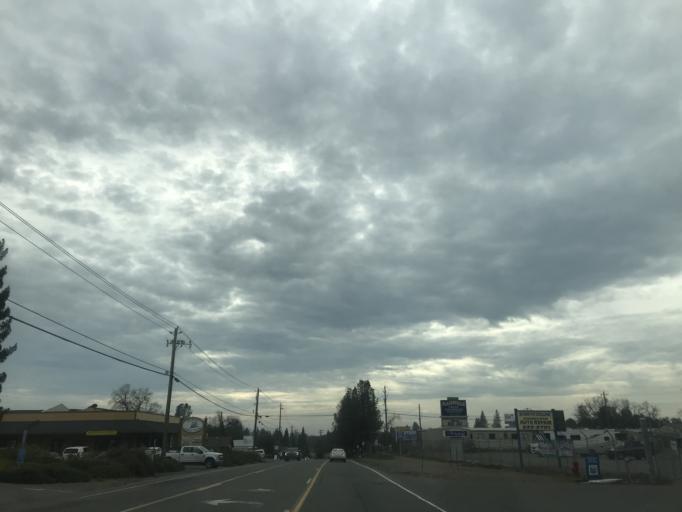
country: US
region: California
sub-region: El Dorado County
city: Diamond Springs
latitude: 38.6975
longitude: -120.8234
